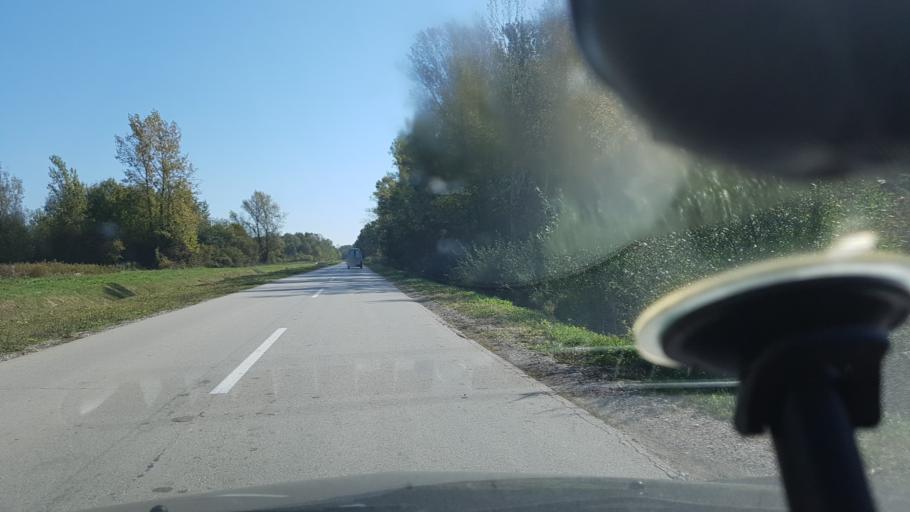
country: HR
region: Zagrebacka
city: Brckovljani
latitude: 45.7655
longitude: 16.2387
